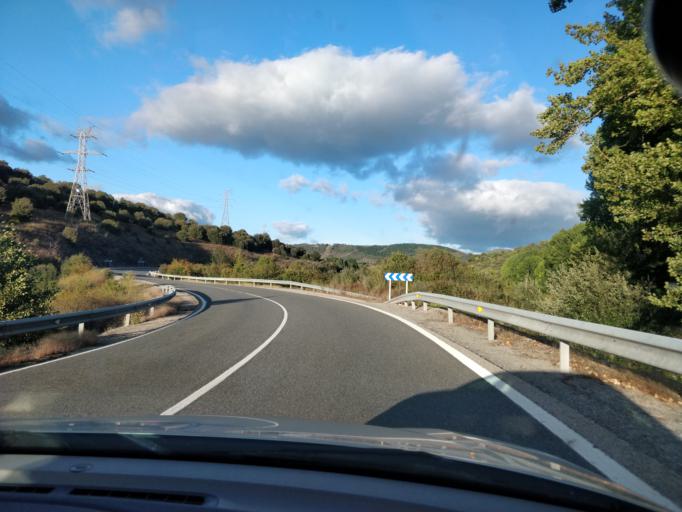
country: ES
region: Castille and Leon
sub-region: Provincia de Leon
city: Carucedo
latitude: 42.4895
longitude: -6.7482
